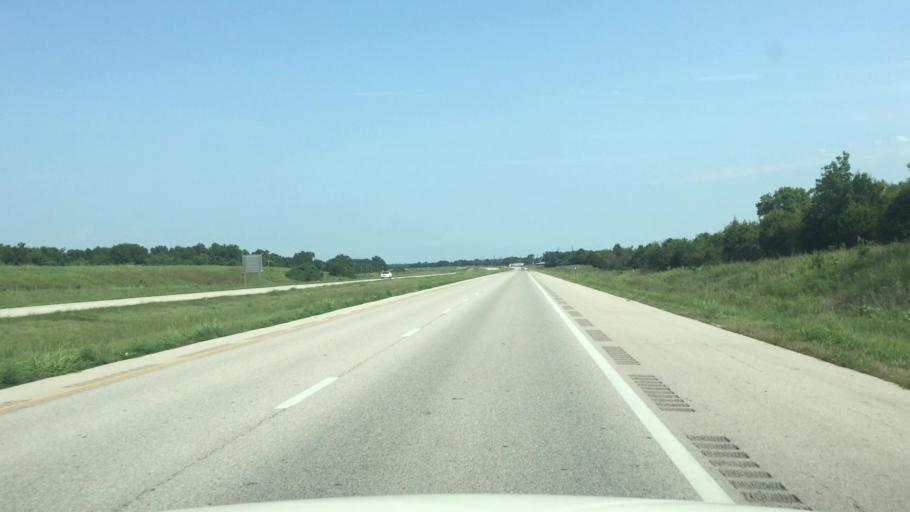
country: US
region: Kansas
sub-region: Montgomery County
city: Coffeyville
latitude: 37.0563
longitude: -95.5816
